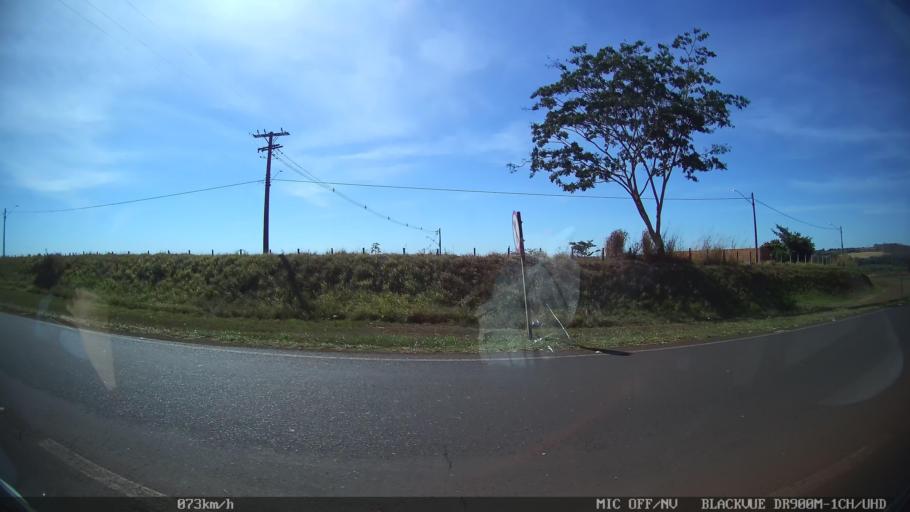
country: BR
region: Sao Paulo
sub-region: Sao Joaquim Da Barra
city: Sao Joaquim da Barra
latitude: -20.5233
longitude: -47.8428
